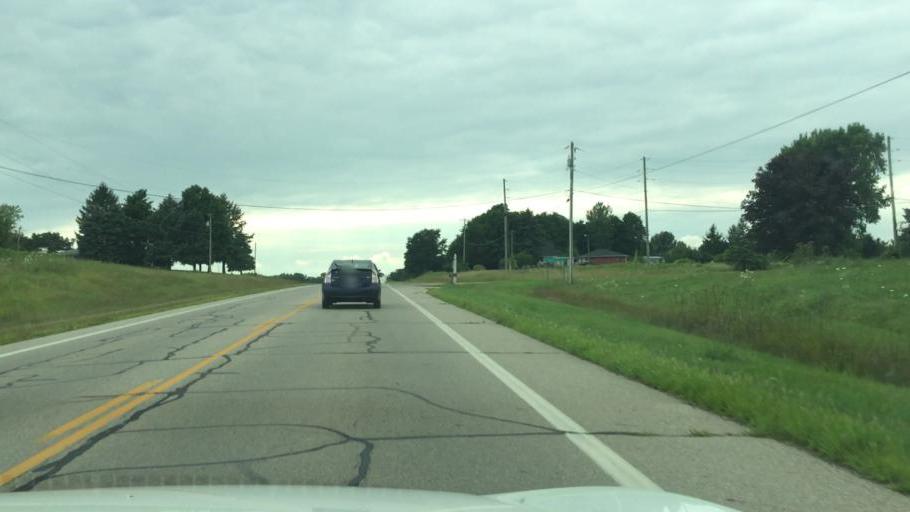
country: US
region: Ohio
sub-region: Champaign County
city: Mechanicsburg
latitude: 40.0784
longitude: -83.6100
